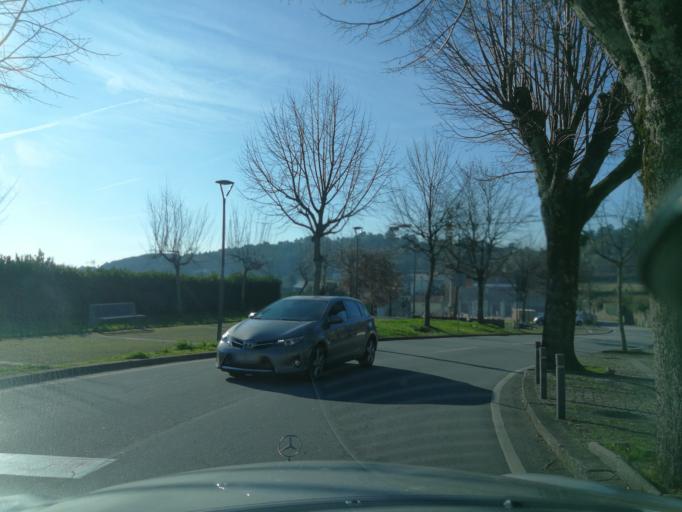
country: PT
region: Braga
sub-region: Braga
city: Adaufe
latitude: 41.5690
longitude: -8.3893
